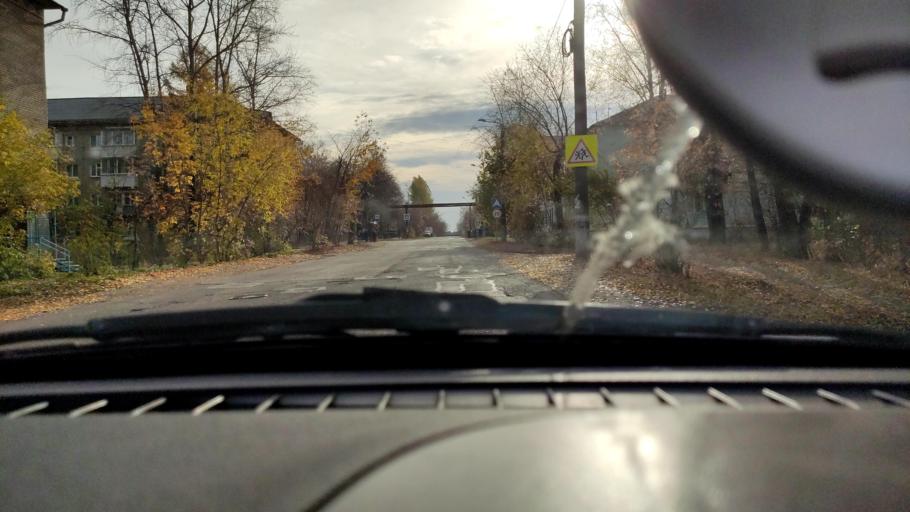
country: RU
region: Perm
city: Perm
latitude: 58.0870
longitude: 56.3906
